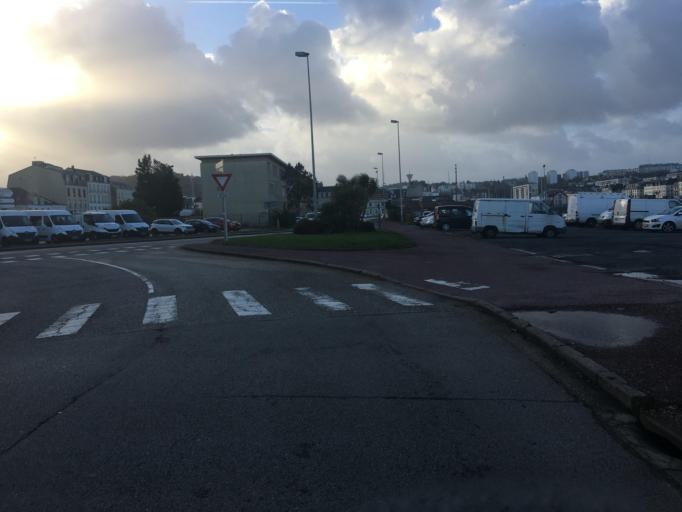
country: FR
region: Lower Normandy
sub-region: Departement de la Manche
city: Cherbourg-Octeville
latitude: 49.6421
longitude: -1.6179
